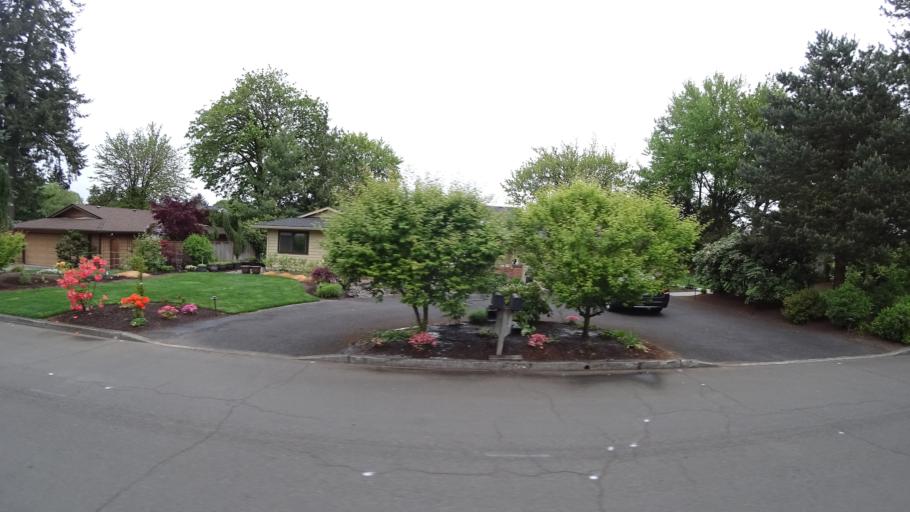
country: US
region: Oregon
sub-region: Washington County
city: Aloha
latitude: 45.5122
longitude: -122.8698
